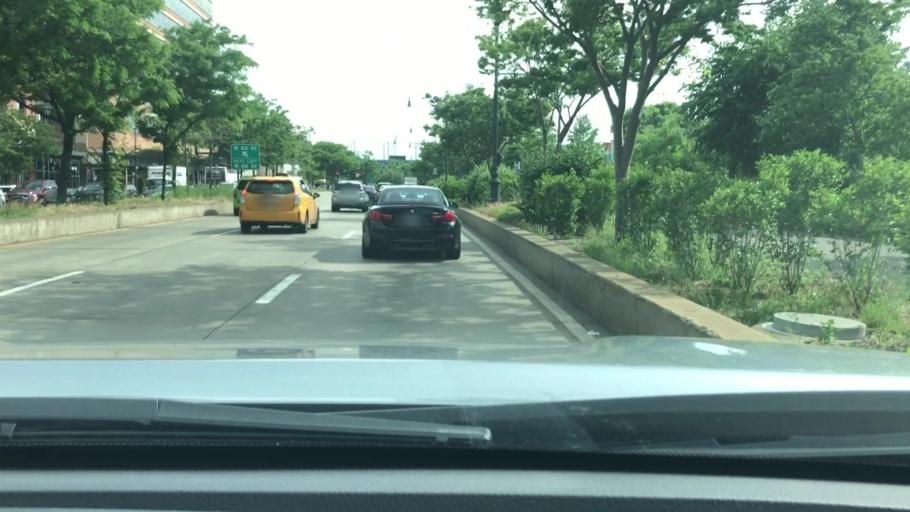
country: US
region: New Jersey
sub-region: Hudson County
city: Weehawken
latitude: 40.7532
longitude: -74.0075
